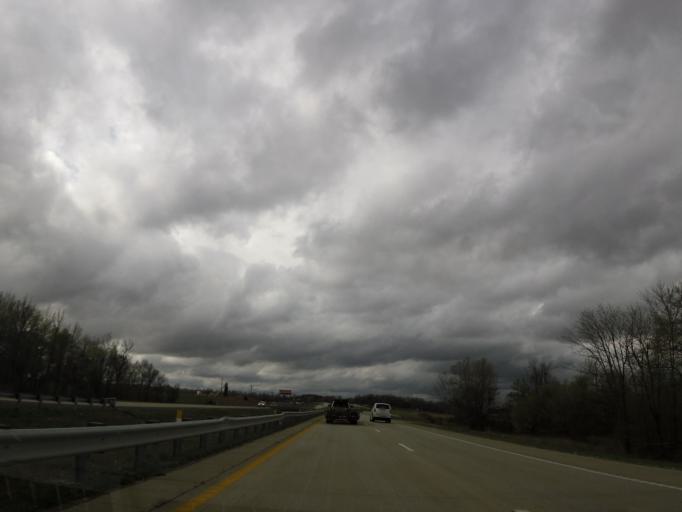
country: US
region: Missouri
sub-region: Butler County
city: Poplar Bluff
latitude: 36.6925
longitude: -90.4805
